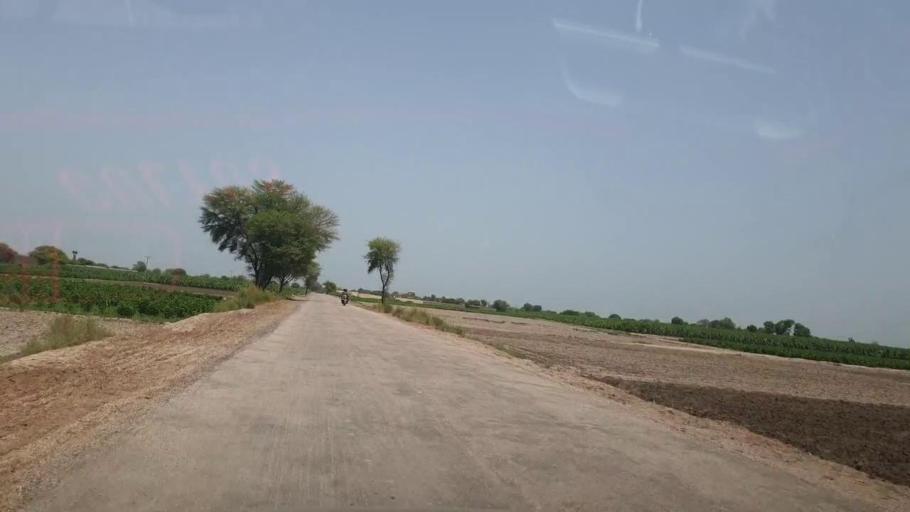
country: PK
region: Sindh
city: Daulatpur
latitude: 26.3881
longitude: 68.0535
